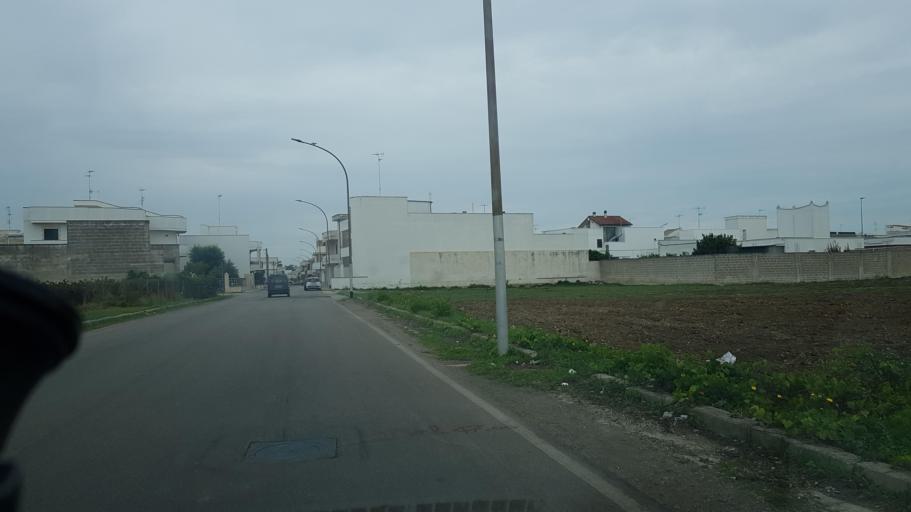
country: IT
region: Apulia
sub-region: Provincia di Lecce
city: Leverano
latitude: 40.2854
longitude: 17.9966
